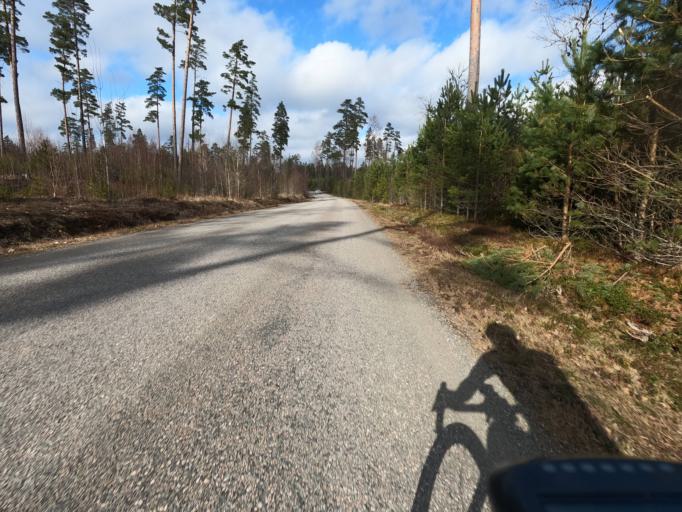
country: SE
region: Kronoberg
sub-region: Alvesta Kommun
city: Vislanda
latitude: 56.7931
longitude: 14.4865
